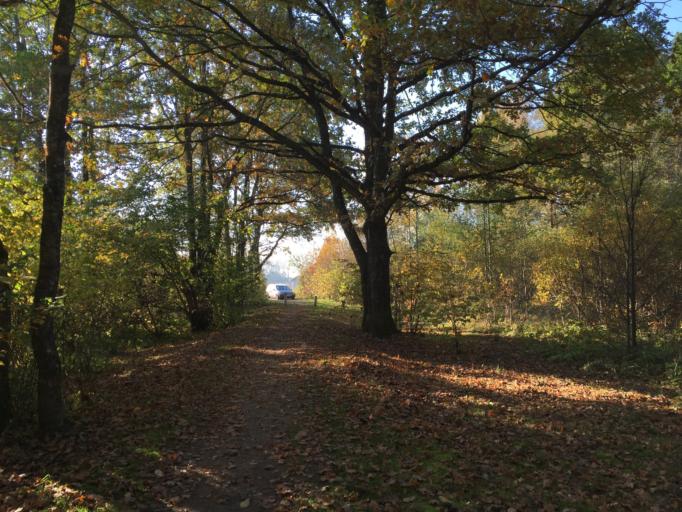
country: LT
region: Klaipedos apskritis
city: Kretinga
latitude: 55.8937
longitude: 21.2092
